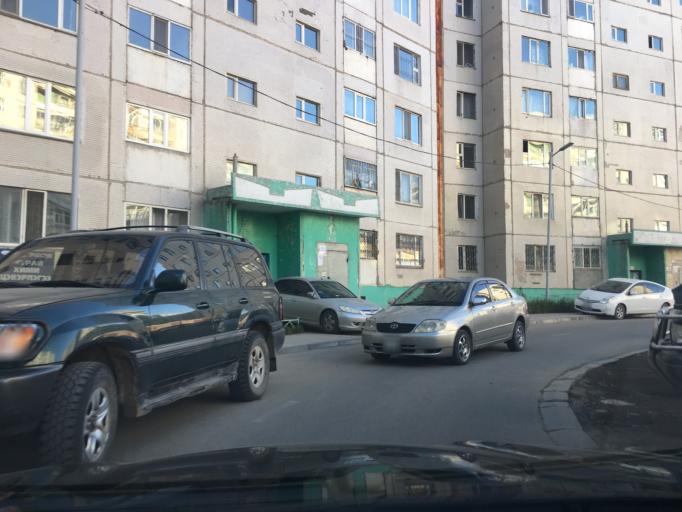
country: MN
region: Ulaanbaatar
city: Ulaanbaatar
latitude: 47.9255
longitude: 106.8784
